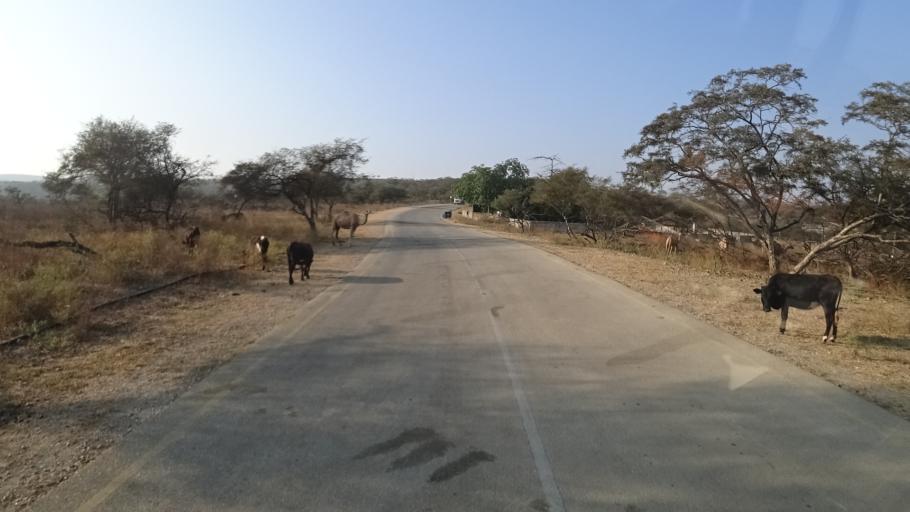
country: YE
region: Al Mahrah
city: Hawf
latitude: 16.7846
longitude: 53.3302
